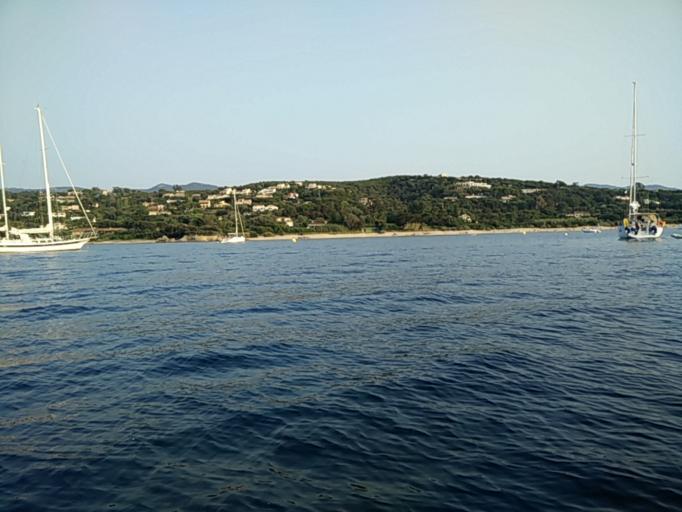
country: FR
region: Corsica
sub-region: Departement de la Corse-du-Sud
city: Pietrosella
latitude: 41.8497
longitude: 8.7726
